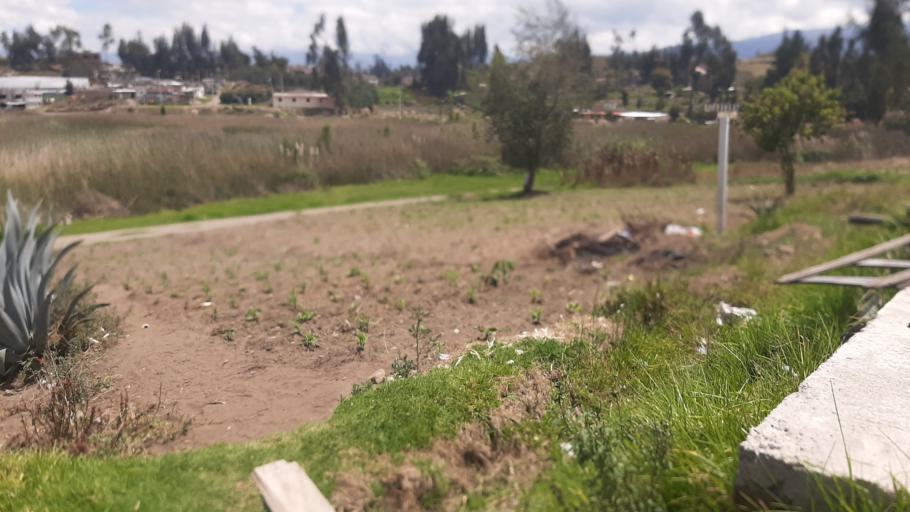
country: EC
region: Chimborazo
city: Riobamba
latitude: -1.6510
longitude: -78.6380
